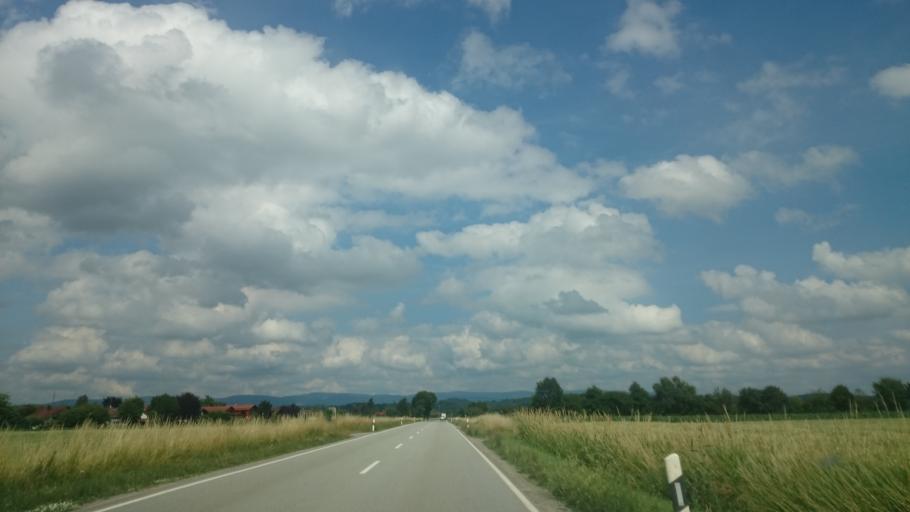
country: DE
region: Bavaria
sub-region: Lower Bavaria
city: Steinach
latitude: 48.9491
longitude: 12.5994
